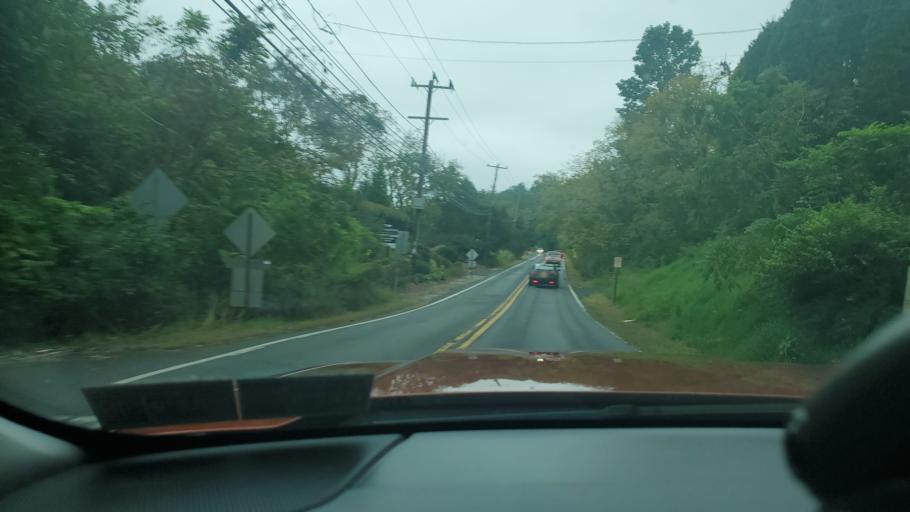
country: US
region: Pennsylvania
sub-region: Montgomery County
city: Woxall
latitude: 40.3246
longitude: -75.4773
